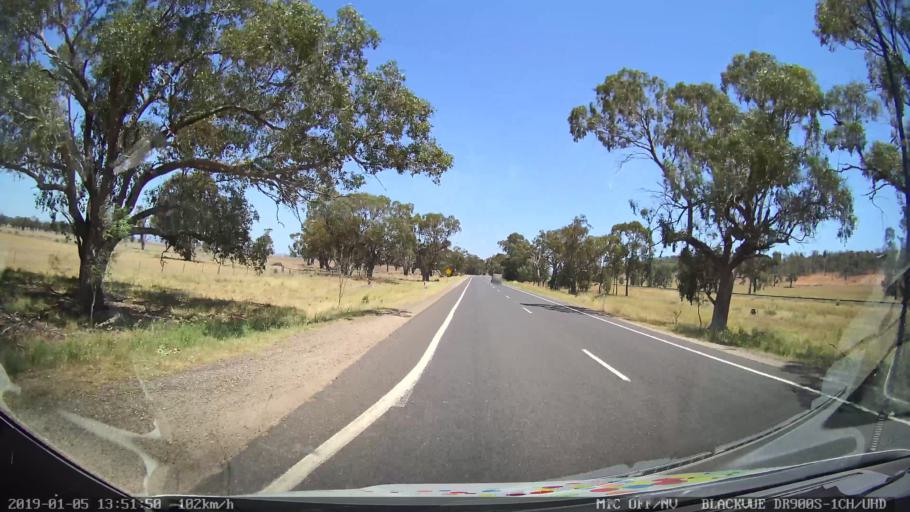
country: AU
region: New South Wales
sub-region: Gunnedah
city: Gunnedah
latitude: -31.0505
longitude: 150.2776
